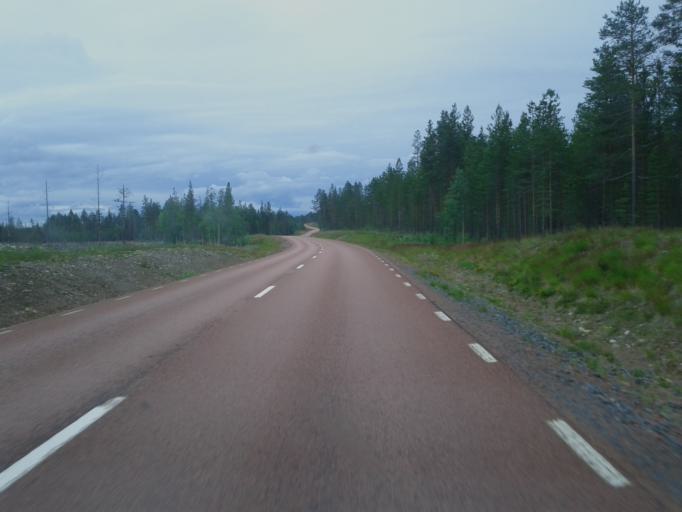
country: NO
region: Hedmark
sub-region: Trysil
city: Innbygda
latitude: 61.6767
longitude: 13.1669
